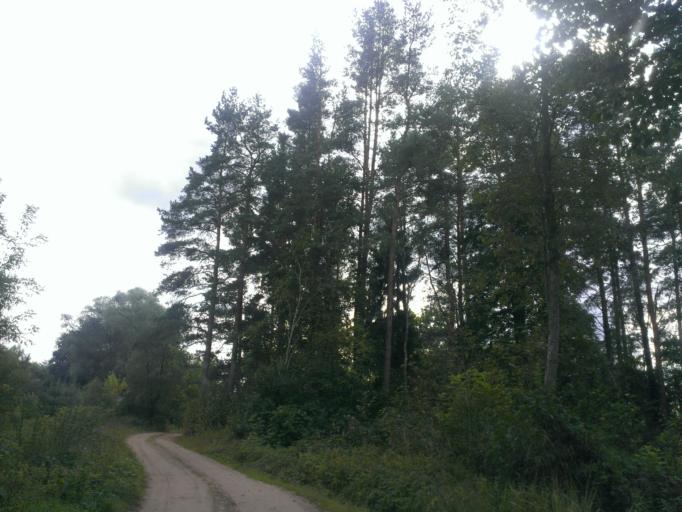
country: LV
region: Garkalne
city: Garkalne
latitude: 56.9722
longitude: 24.4847
